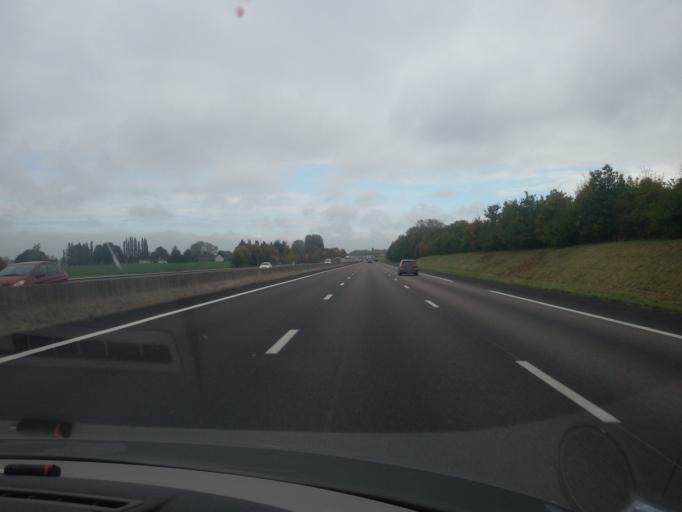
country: FR
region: Haute-Normandie
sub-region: Departement de l'Eure
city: Hauville
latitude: 49.3715
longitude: 0.6969
